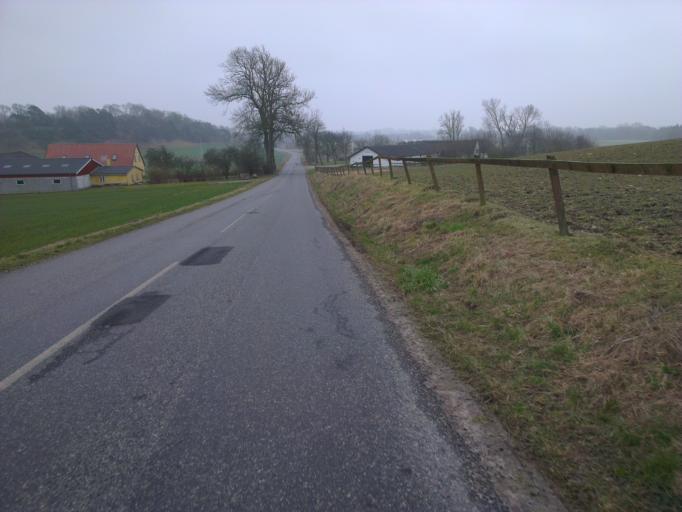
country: DK
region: Capital Region
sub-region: Frederikssund Kommune
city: Skibby
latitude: 55.7737
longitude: 12.0221
